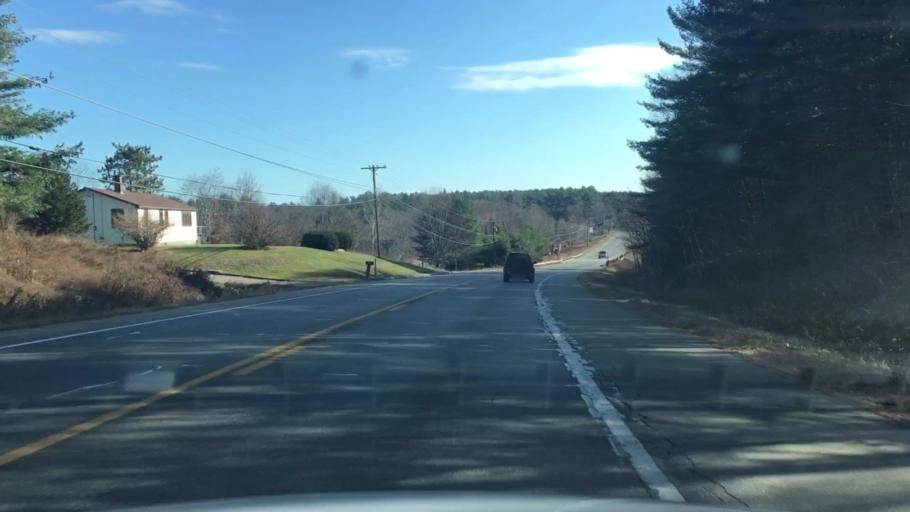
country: US
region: Maine
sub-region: Kennebec County
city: Windsor
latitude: 44.2678
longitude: -69.5662
